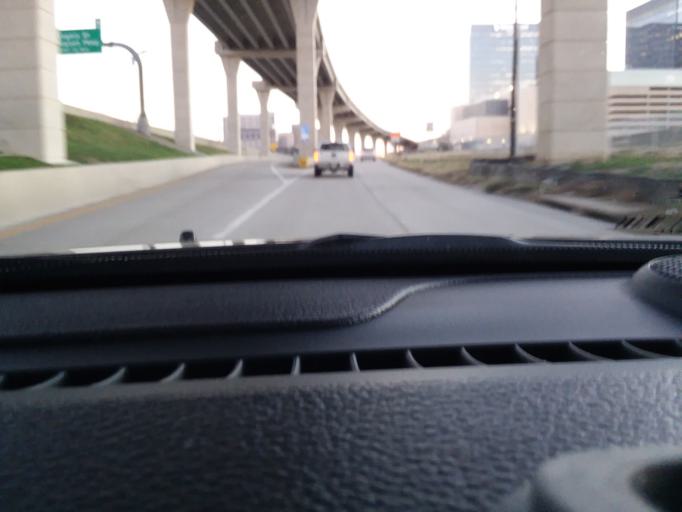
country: US
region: Texas
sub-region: Collin County
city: Frisco
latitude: 33.0884
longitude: -96.8233
